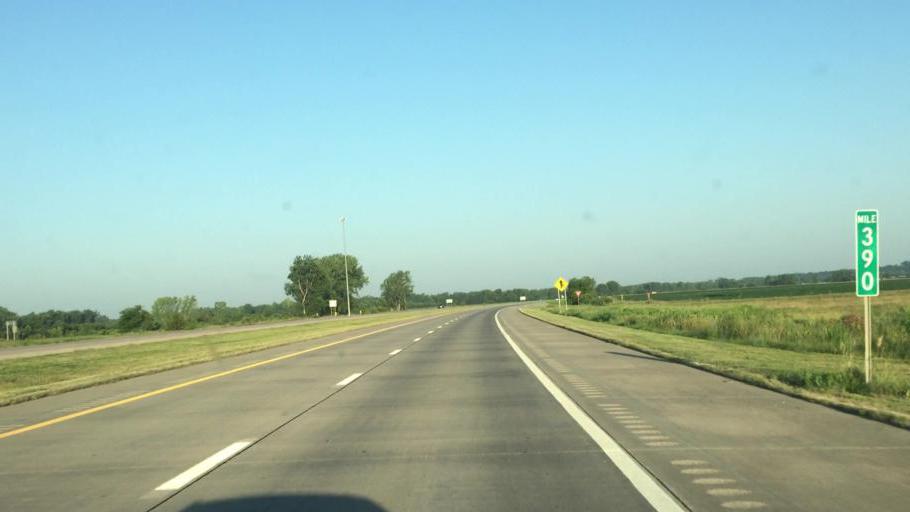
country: US
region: Kansas
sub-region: Doniphan County
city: Elwood
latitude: 39.7410
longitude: -94.8950
